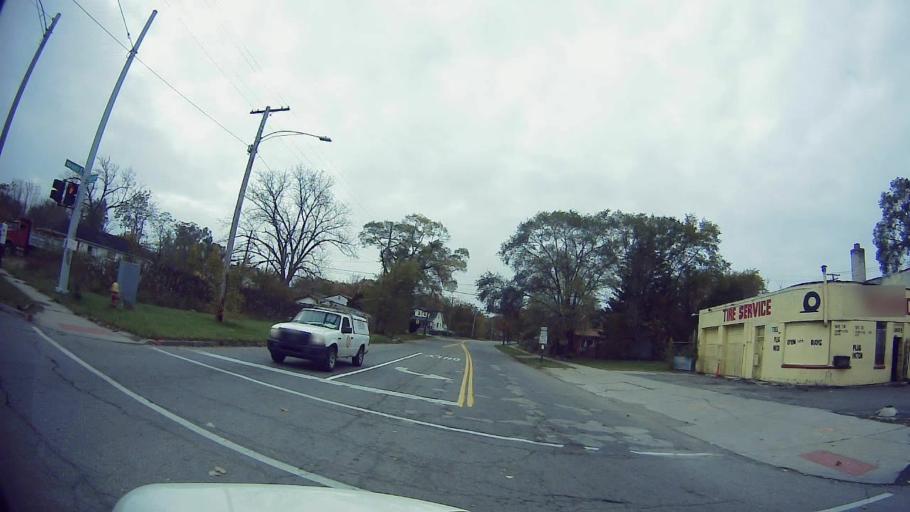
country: US
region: Michigan
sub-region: Wayne County
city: Highland Park
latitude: 42.4254
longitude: -83.0826
